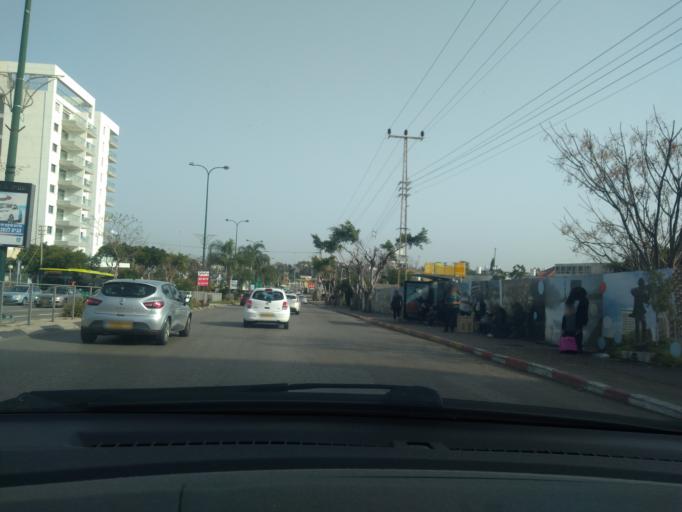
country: IL
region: Central District
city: Netanya
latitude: 32.3264
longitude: 34.8630
